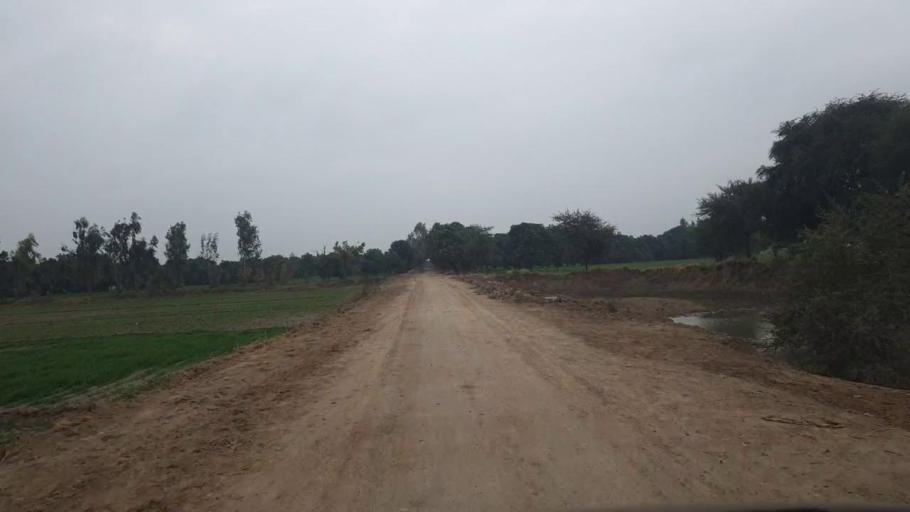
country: PK
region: Sindh
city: Shahdadpur
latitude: 25.8626
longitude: 68.6980
